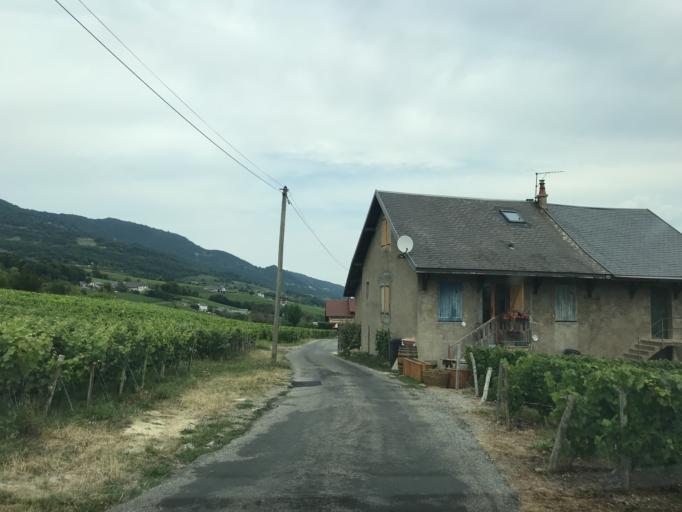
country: FR
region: Rhone-Alpes
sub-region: Departement de la Savoie
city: Saint-Baldoph
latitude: 45.4981
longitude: 5.9583
